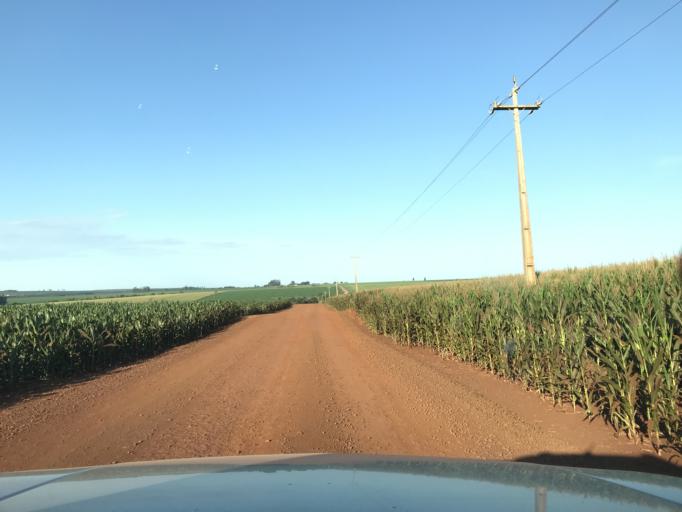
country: BR
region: Parana
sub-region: Palotina
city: Palotina
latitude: -24.2532
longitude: -53.7367
